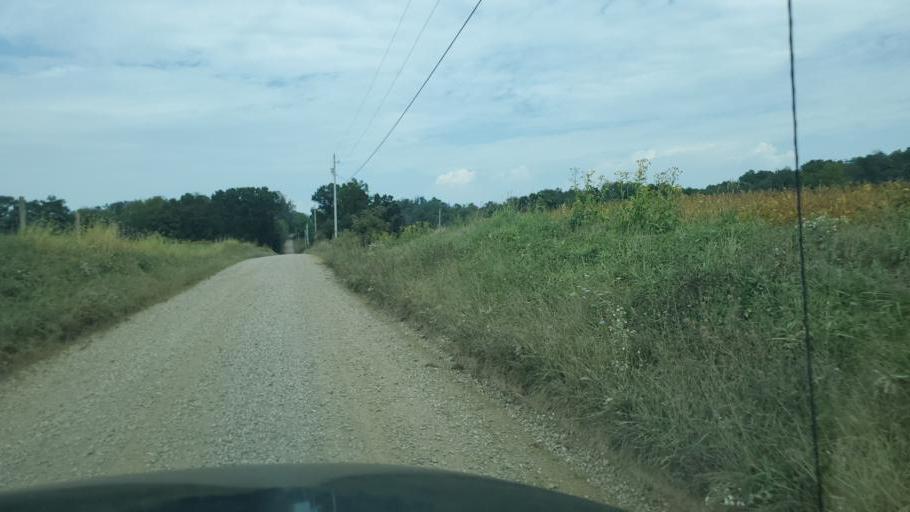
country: US
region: Ohio
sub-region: Perry County
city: Somerset
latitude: 39.9625
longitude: -82.2135
